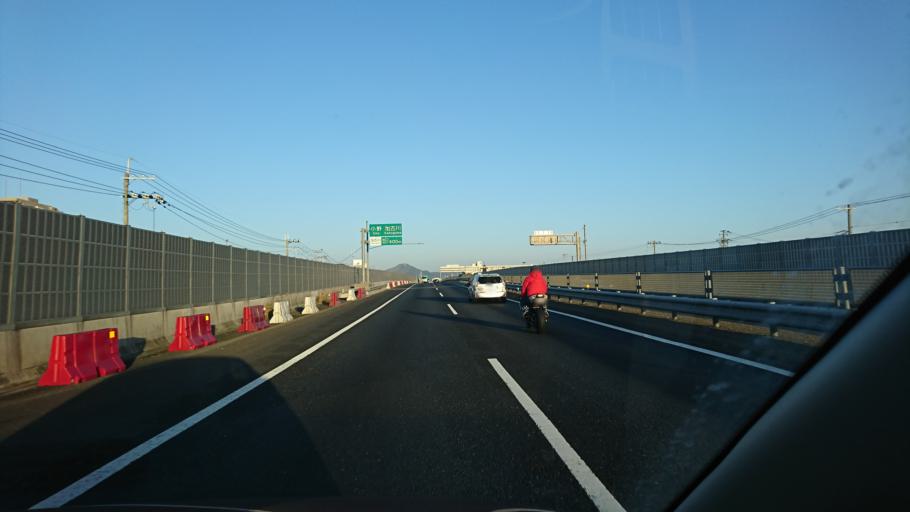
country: JP
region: Hyogo
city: Kakogawacho-honmachi
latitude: 34.7661
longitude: 134.8498
